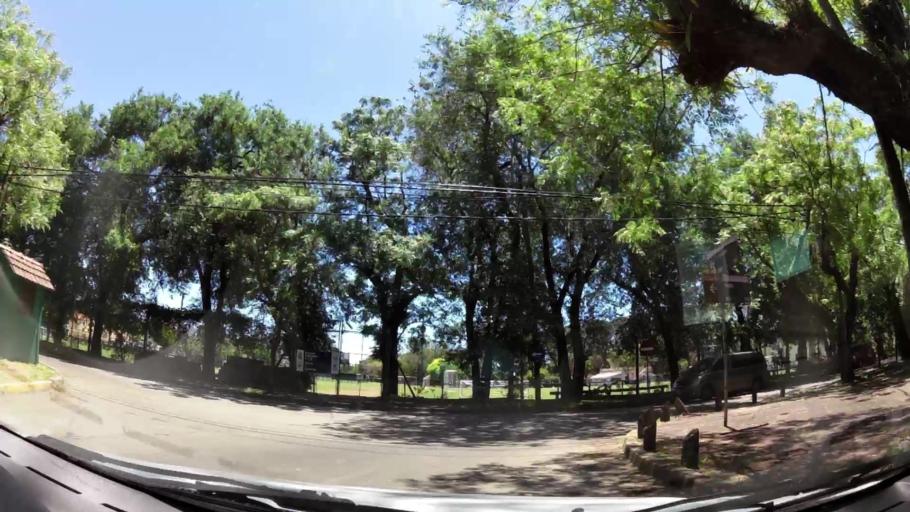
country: AR
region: Buenos Aires
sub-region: Partido de San Isidro
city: San Isidro
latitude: -34.4738
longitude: -58.5047
